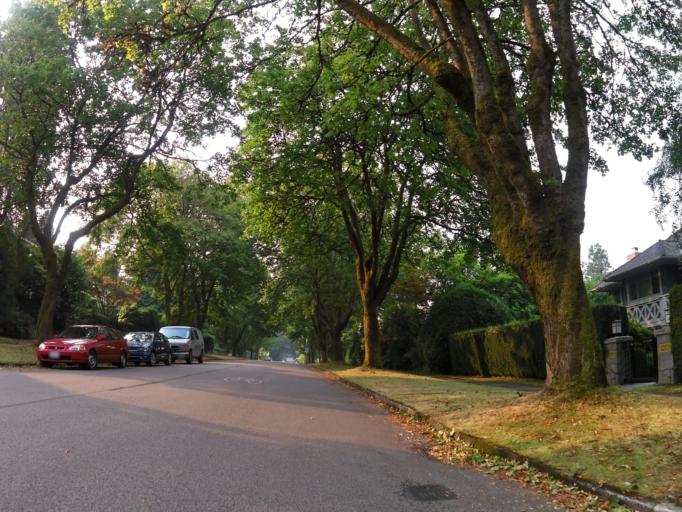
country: CA
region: British Columbia
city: Vancouver
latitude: 49.2436
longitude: -123.1456
